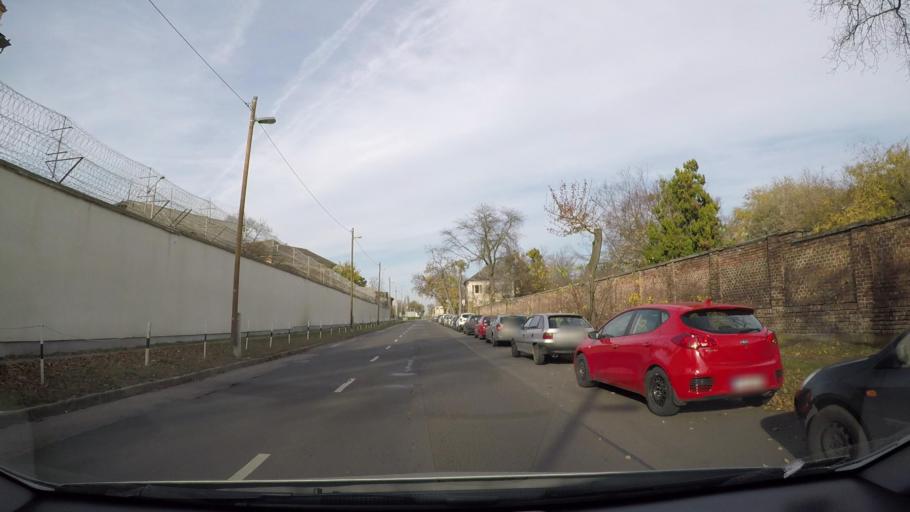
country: HU
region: Budapest
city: Budapest X. keruelet
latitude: 47.4706
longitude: 19.1785
